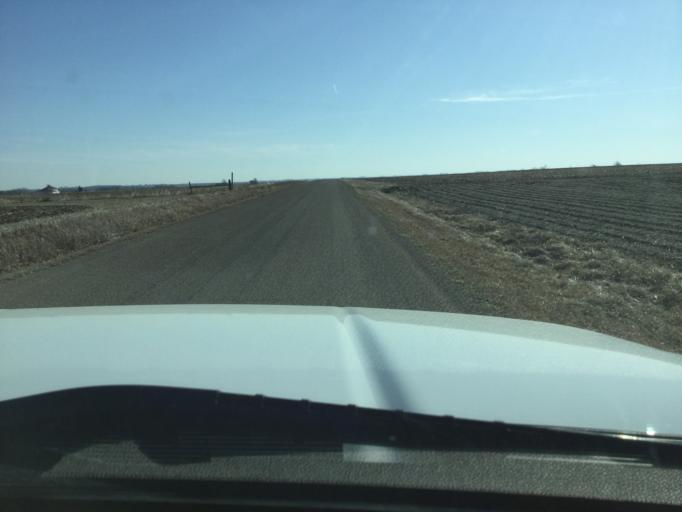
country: US
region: Kansas
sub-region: Brown County
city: Horton
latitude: 39.7256
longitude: -95.4445
